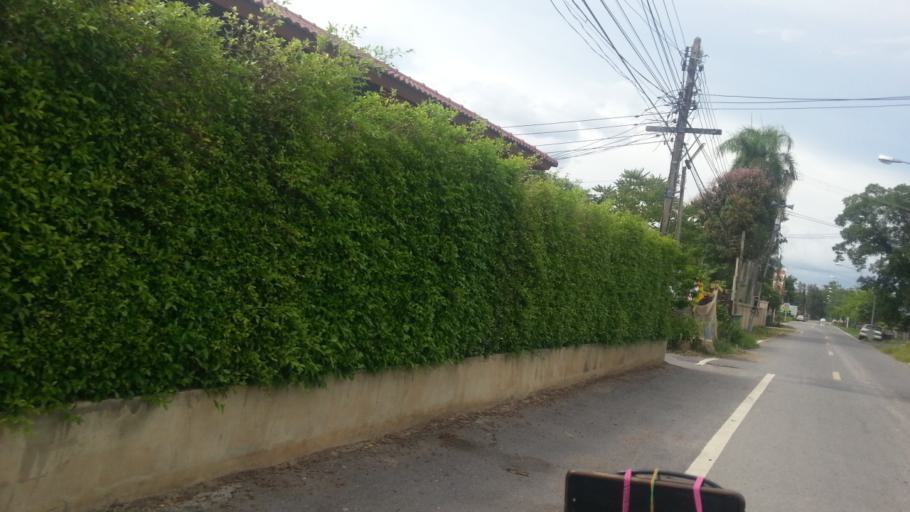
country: TH
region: Pathum Thani
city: Nong Suea
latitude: 14.1290
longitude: 100.8234
